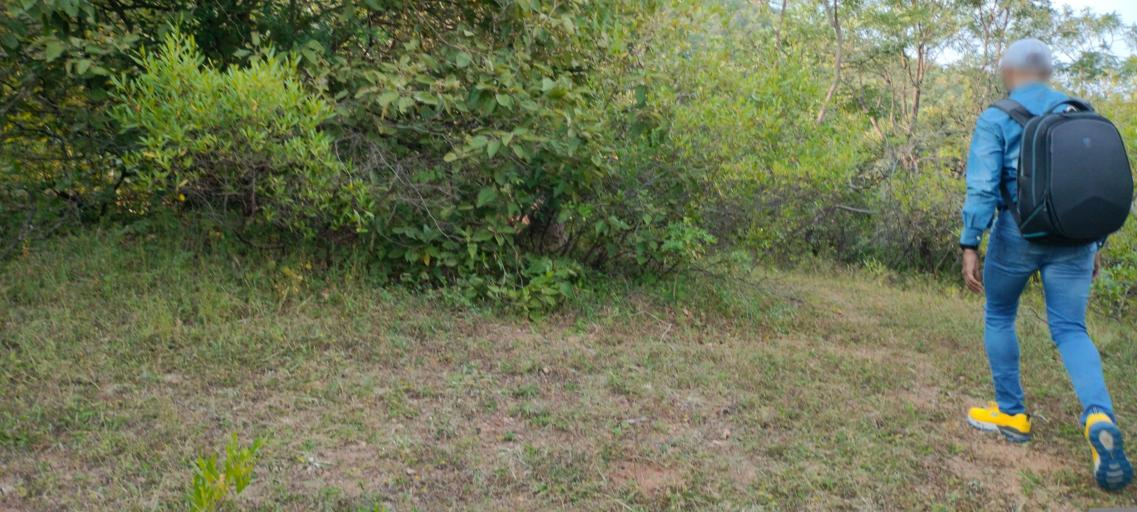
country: IN
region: Telangana
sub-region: Mahbubnagar
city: Farrukhnagar
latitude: 16.8923
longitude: 78.4961
